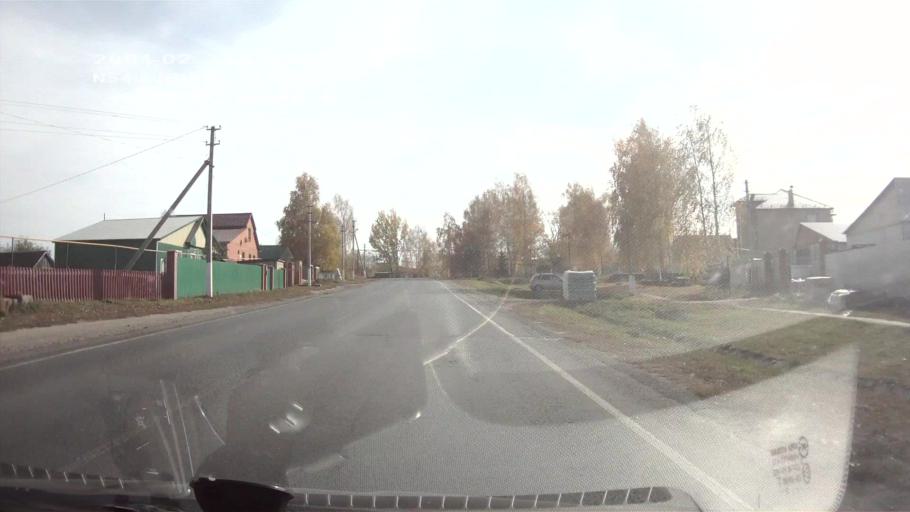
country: RU
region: Mordoviya
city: Turgenevo
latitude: 54.8449
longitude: 46.3479
